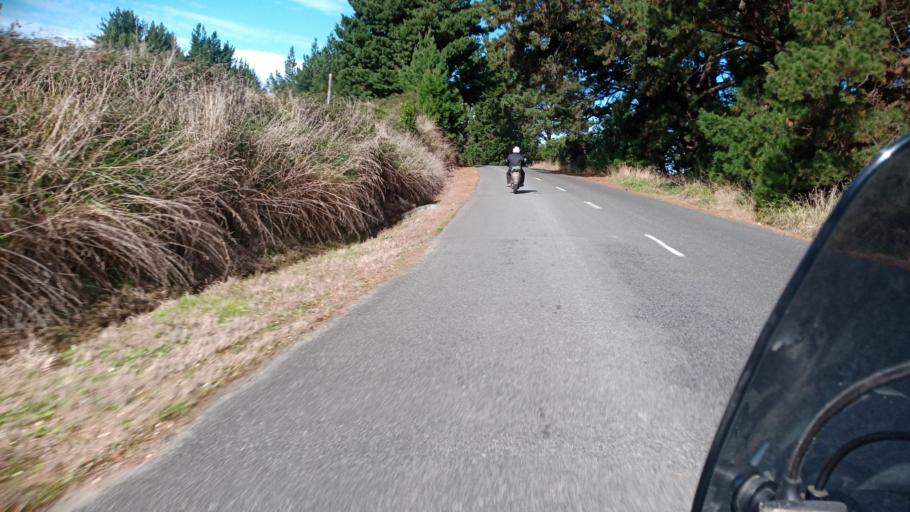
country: NZ
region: Hawke's Bay
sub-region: Wairoa District
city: Wairoa
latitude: -39.0441
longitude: 177.1126
